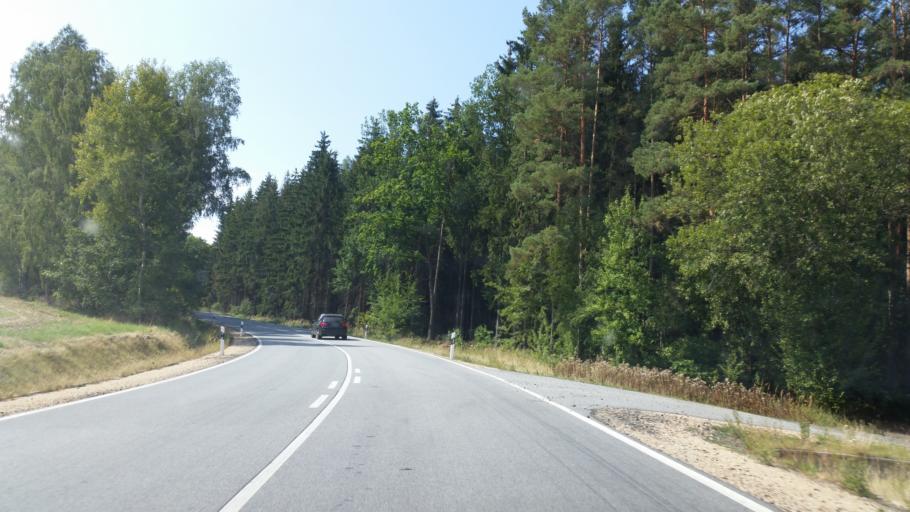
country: DE
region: Saxony
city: Grosshennersdorf
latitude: 50.9798
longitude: 14.7559
